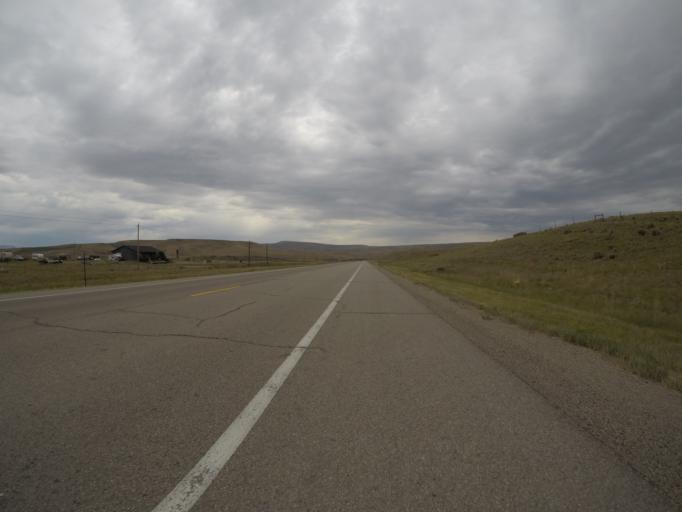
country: US
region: Wyoming
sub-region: Lincoln County
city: Kemmerer
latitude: 41.7972
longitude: -110.5674
